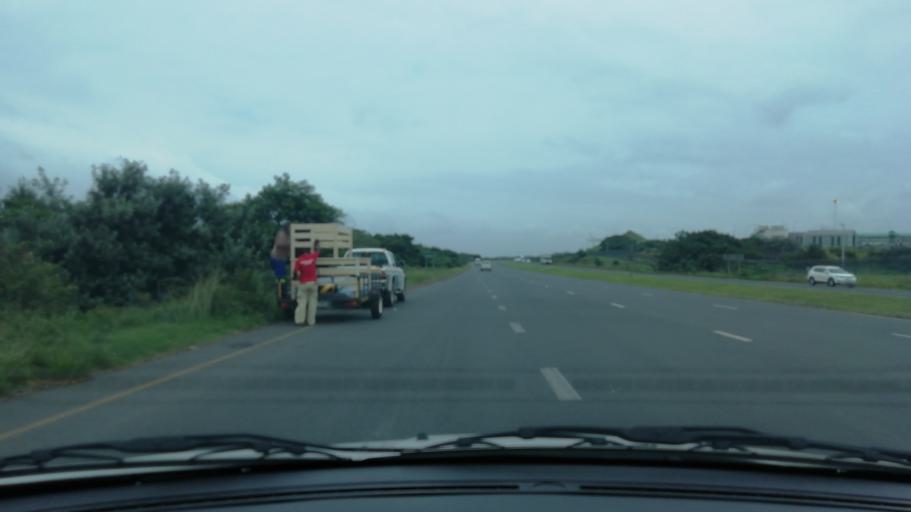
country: ZA
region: KwaZulu-Natal
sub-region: uThungulu District Municipality
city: Richards Bay
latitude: -28.7711
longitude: 32.0316
